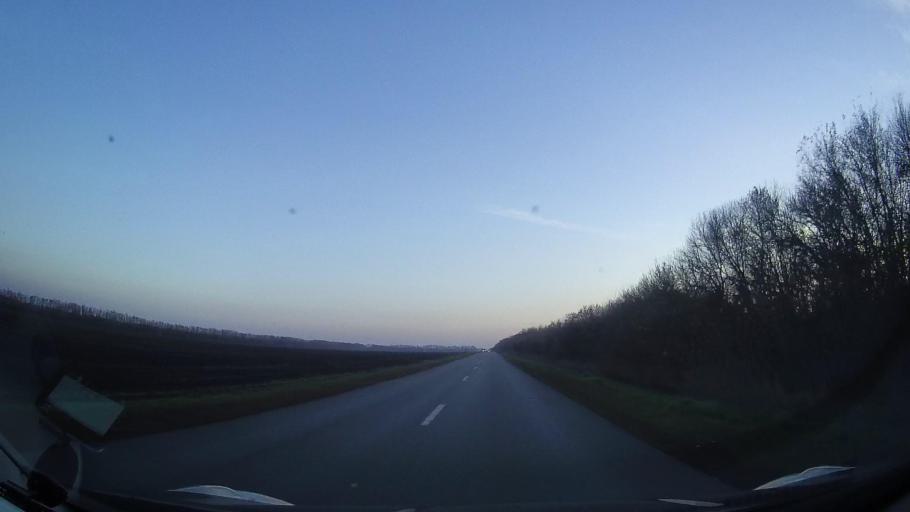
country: RU
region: Rostov
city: Zernograd
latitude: 47.0238
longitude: 40.3917
